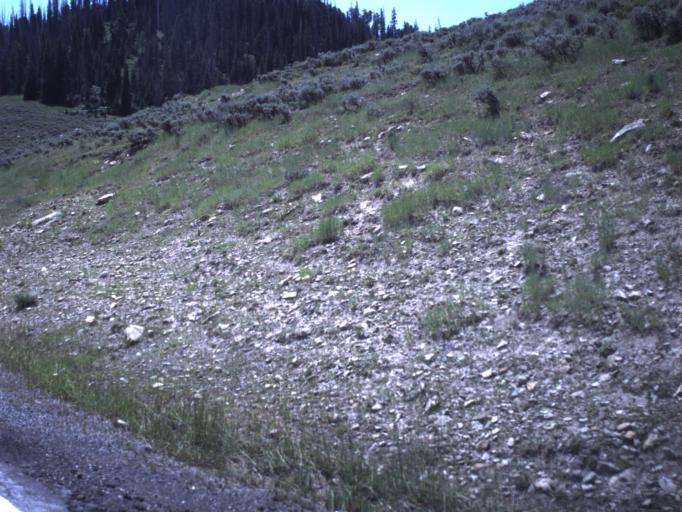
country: US
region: Utah
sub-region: Sanpete County
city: Fairview
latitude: 39.6640
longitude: -111.2439
